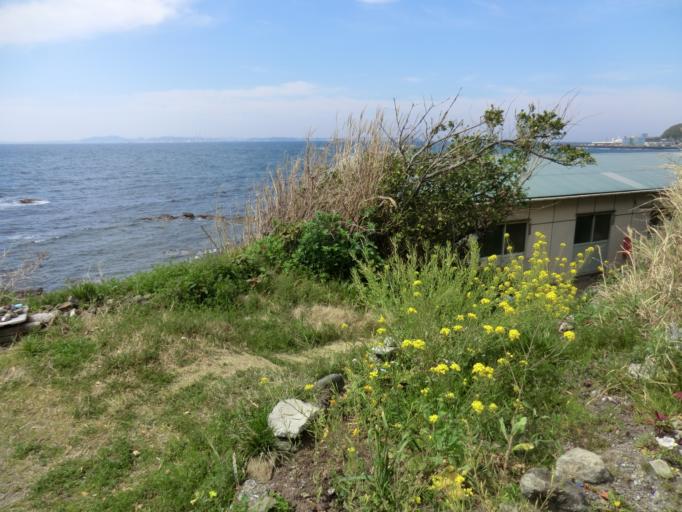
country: JP
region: Chiba
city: Futtsu
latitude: 35.1614
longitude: 139.8195
